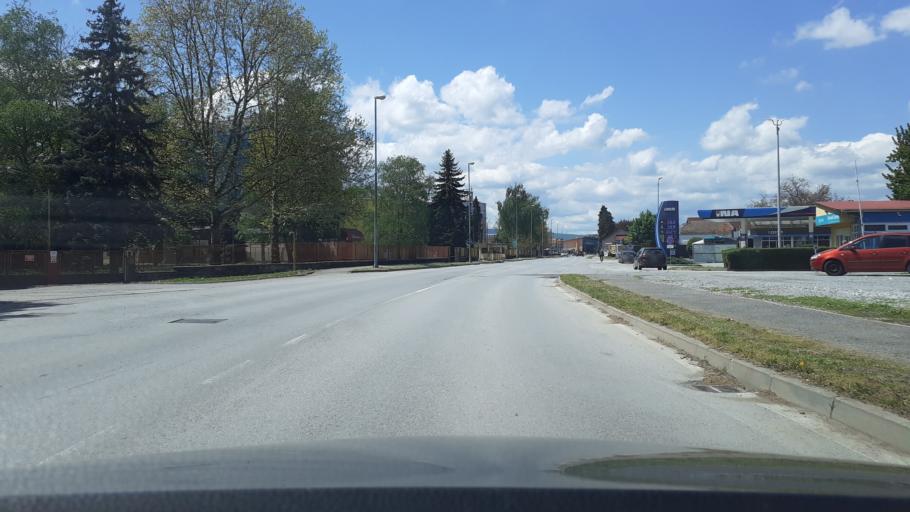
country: HR
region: Pozesko-Slavonska
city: Pozega
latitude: 45.3389
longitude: 17.6885
